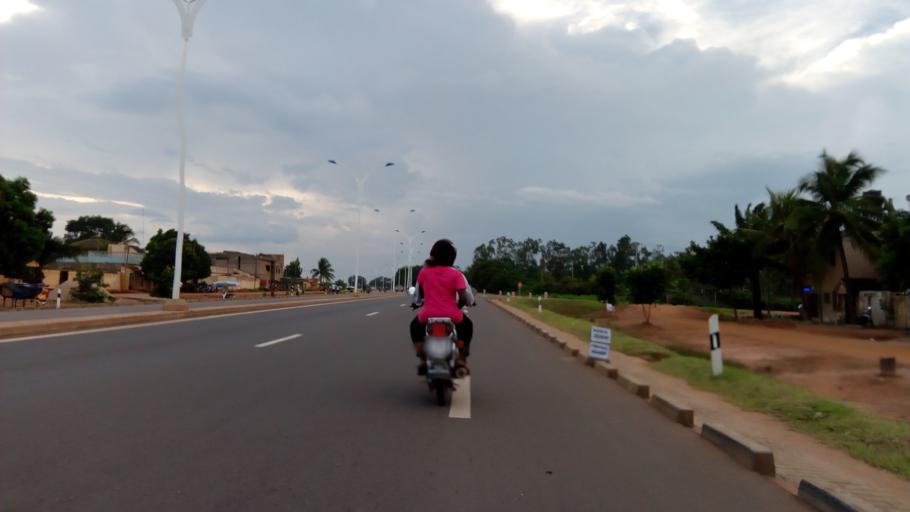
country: TG
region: Maritime
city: Lome
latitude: 6.2442
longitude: 1.1928
